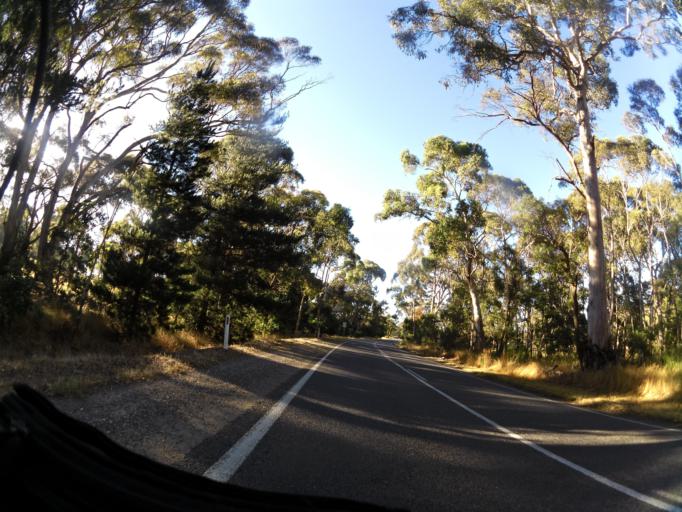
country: AU
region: Victoria
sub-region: Ballarat North
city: Delacombe
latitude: -37.4493
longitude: 143.3804
